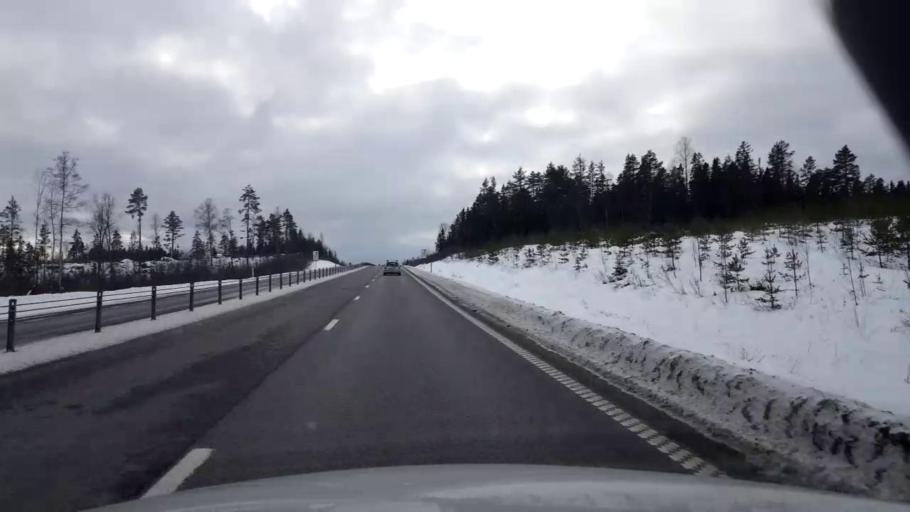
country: SE
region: Vaesternorrland
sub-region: Sundsvalls Kommun
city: Njurundabommen
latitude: 62.1017
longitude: 17.3111
